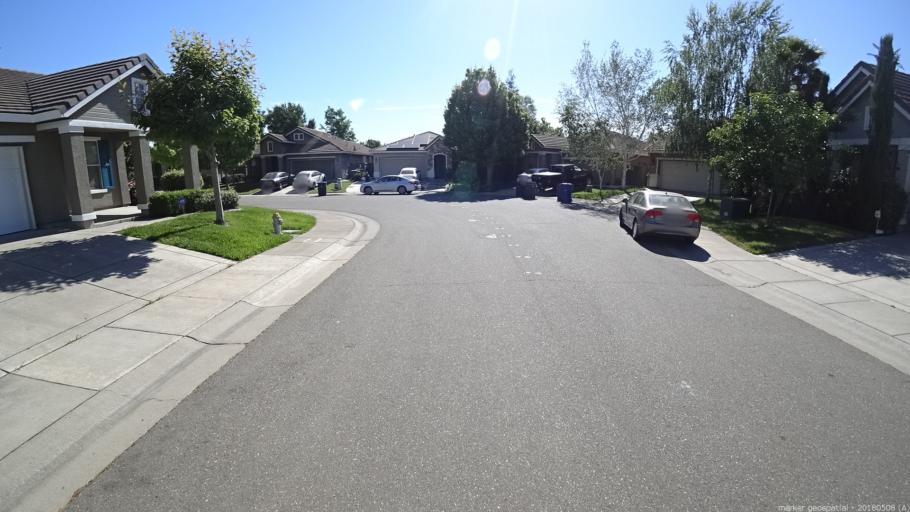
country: US
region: California
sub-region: Sacramento County
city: Elverta
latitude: 38.6827
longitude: -121.4978
